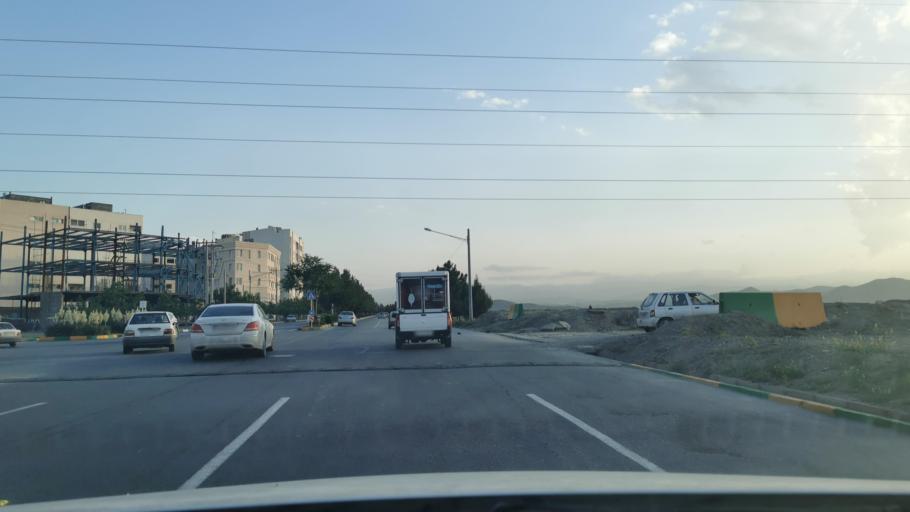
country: IR
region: Razavi Khorasan
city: Mashhad
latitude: 36.3908
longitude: 59.4697
